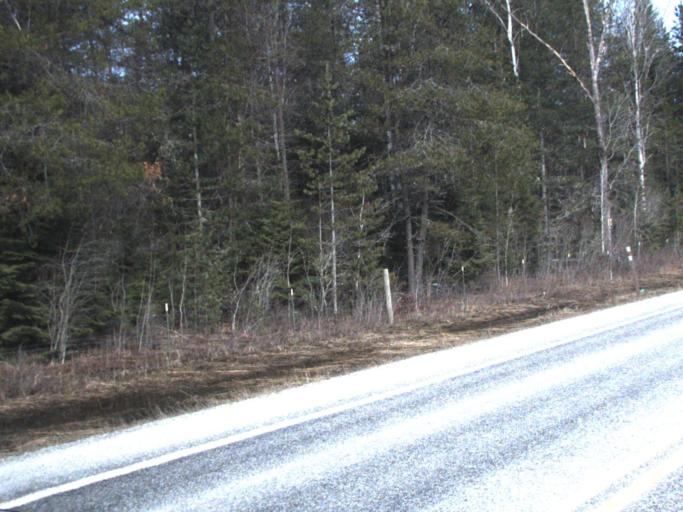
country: US
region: Washington
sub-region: Stevens County
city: Chewelah
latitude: 48.6378
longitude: -117.3710
